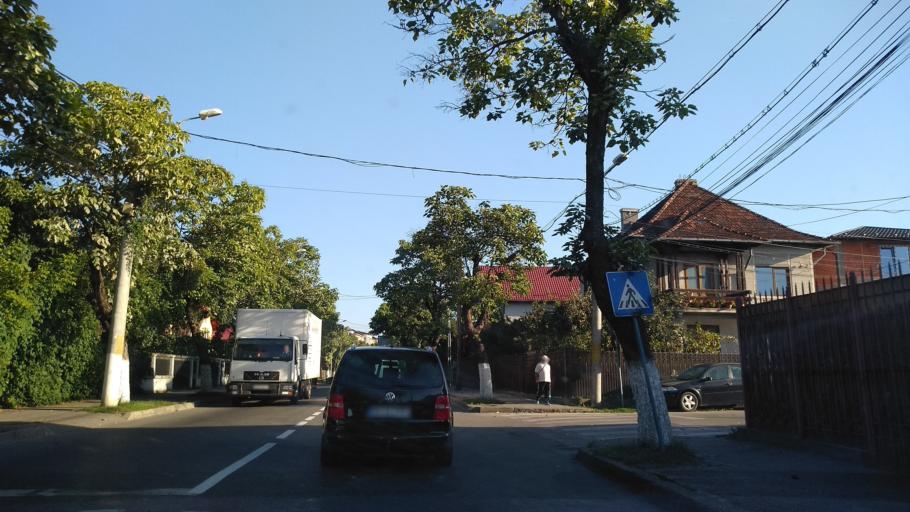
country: RO
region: Arges
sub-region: Municipiul Curtea de Arges
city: Curtea de Arges
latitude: 45.1592
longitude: 24.6718
